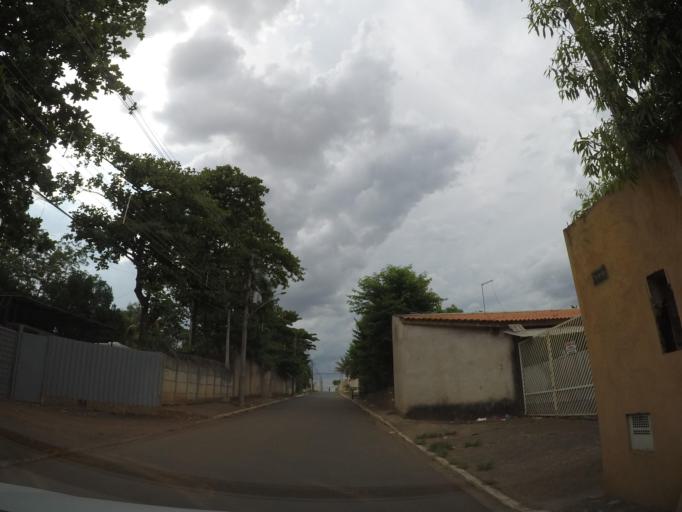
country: BR
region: Sao Paulo
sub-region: Sumare
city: Sumare
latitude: -22.8148
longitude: -47.2451
